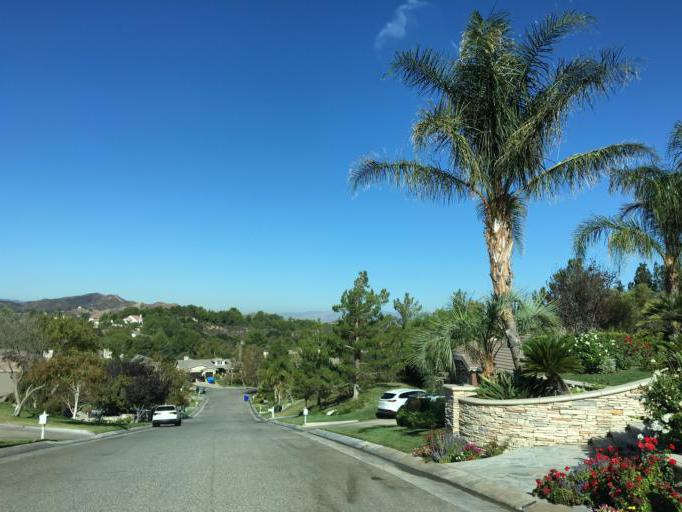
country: US
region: California
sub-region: Los Angeles County
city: Agua Dulce
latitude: 34.4015
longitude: -118.4034
